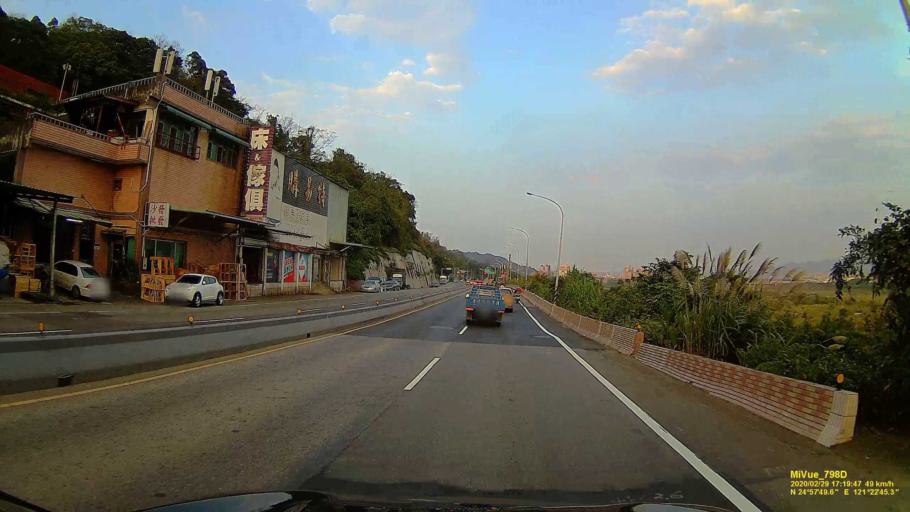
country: TW
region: Taiwan
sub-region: Taoyuan
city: Taoyuan
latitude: 24.9639
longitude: 121.3795
